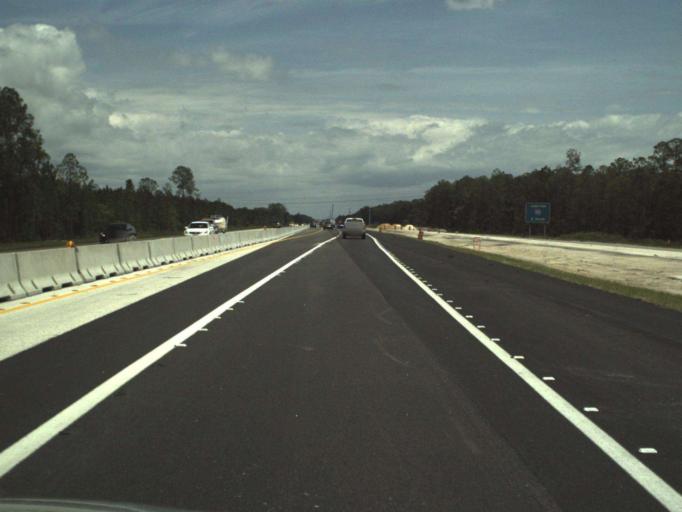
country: US
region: Florida
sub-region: Volusia County
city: Samsula-Spruce Creek
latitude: 29.1410
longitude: -81.1098
